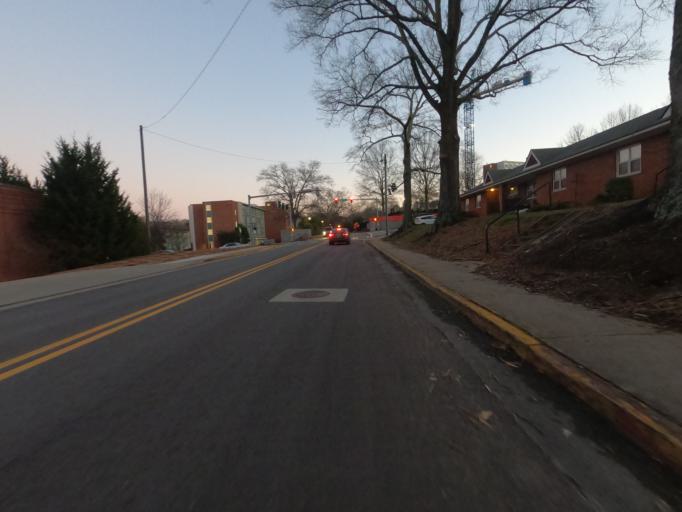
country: US
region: Georgia
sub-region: Clarke County
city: Athens
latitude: 33.9517
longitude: -83.3793
